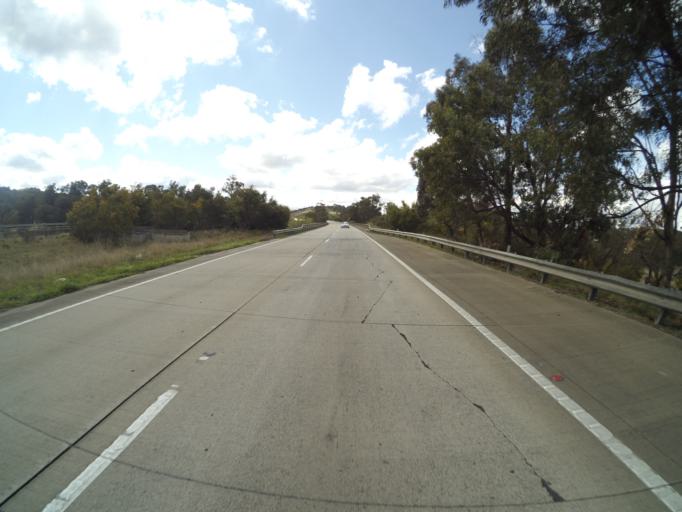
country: AU
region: New South Wales
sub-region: Wingecarribee
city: Bowral
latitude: -34.4655
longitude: 150.3485
